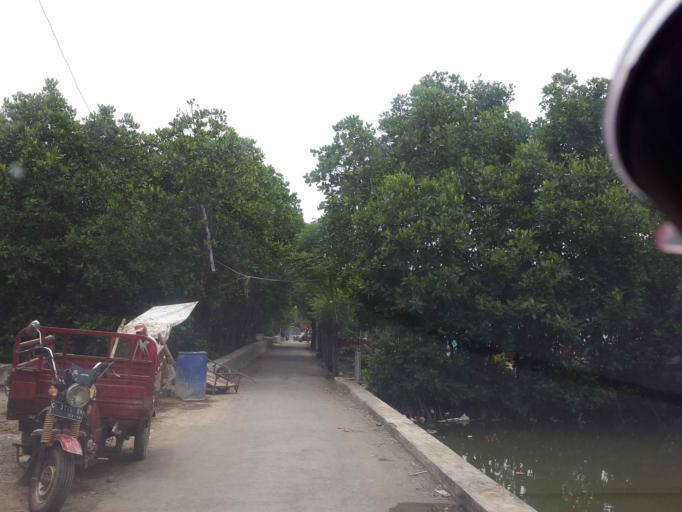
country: ID
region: Central Java
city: Tegal
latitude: -6.8467
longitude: 109.1132
